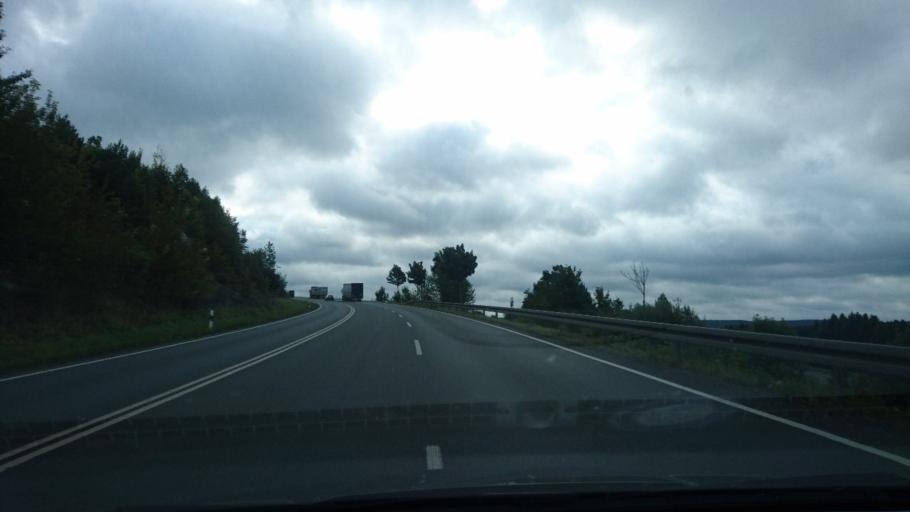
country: DE
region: Bavaria
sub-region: Upper Franconia
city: Selbitz
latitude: 50.3195
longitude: 11.7286
